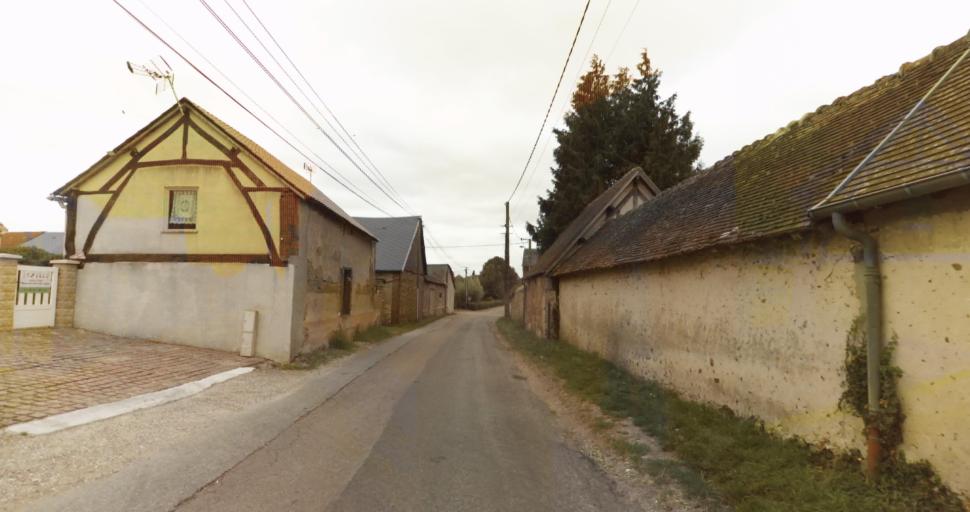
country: FR
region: Haute-Normandie
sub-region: Departement de l'Eure
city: Pacy-sur-Eure
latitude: 48.9515
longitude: 1.3036
